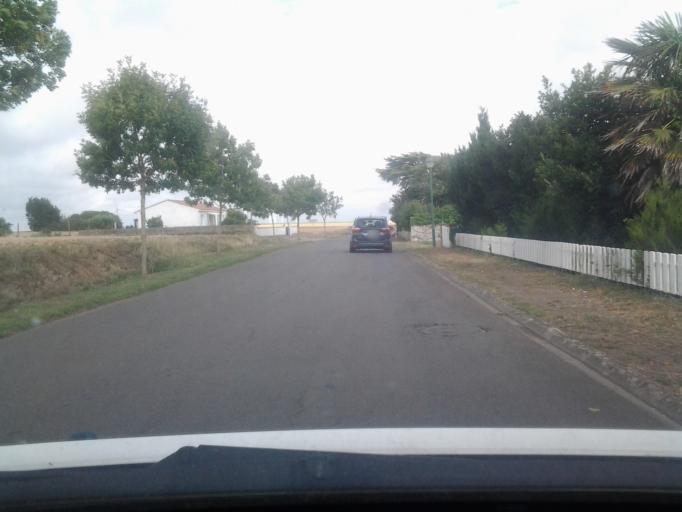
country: FR
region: Pays de la Loire
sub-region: Departement de la Vendee
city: Longeville-sur-Mer
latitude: 46.4225
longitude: -1.4829
